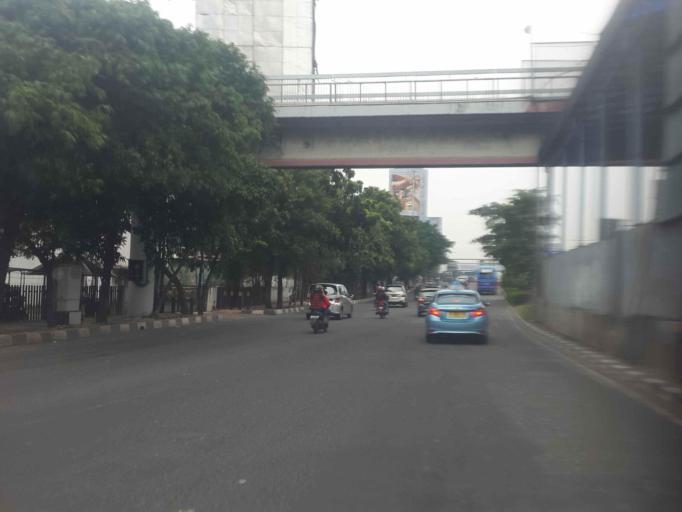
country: ID
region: Jakarta Raya
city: Jakarta
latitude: -6.2407
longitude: 106.8349
